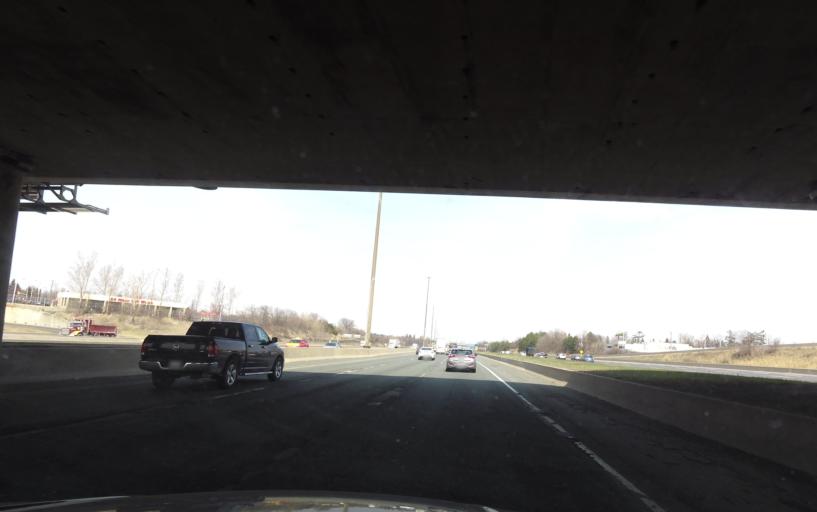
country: CA
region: Ontario
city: Pickering
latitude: 43.7974
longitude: -79.1447
